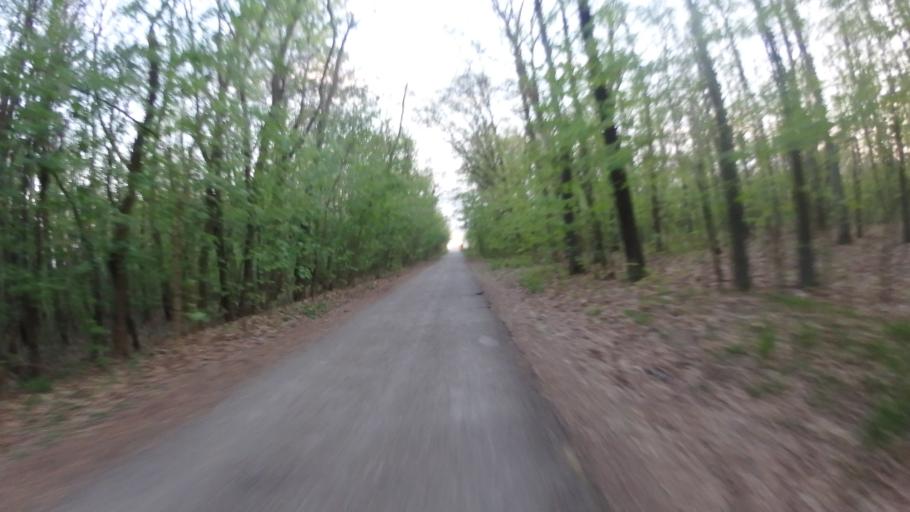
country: CZ
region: South Moravian
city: Ostopovice
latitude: 49.1833
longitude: 16.5549
